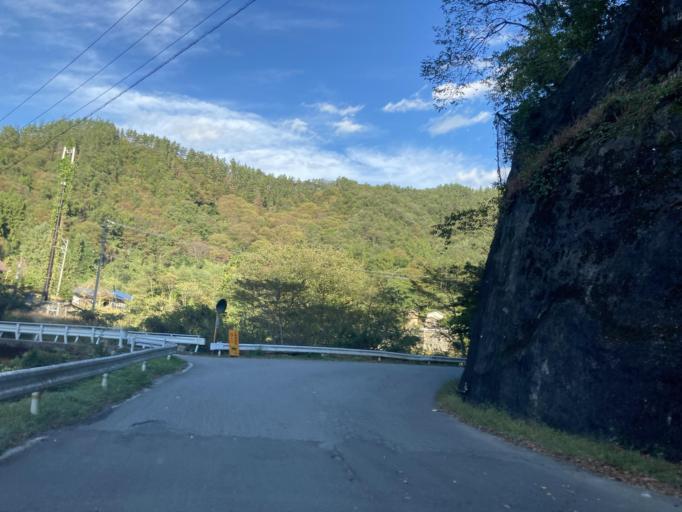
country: JP
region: Nagano
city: Omachi
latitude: 36.4602
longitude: 137.9622
